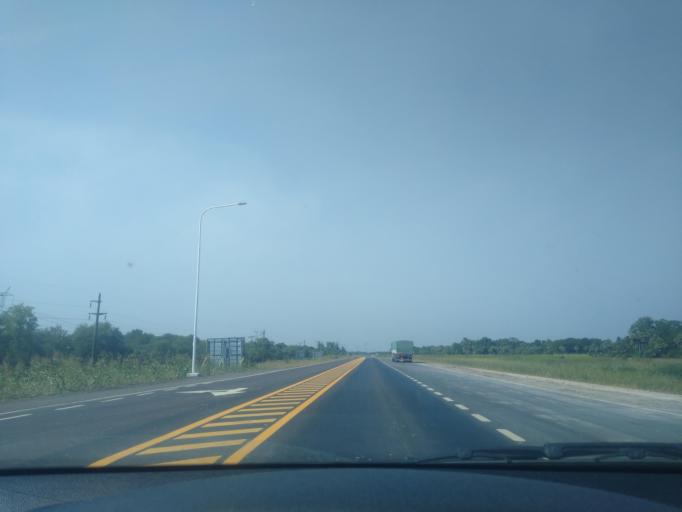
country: AR
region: Chaco
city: Fontana
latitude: -27.5755
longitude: -59.1570
